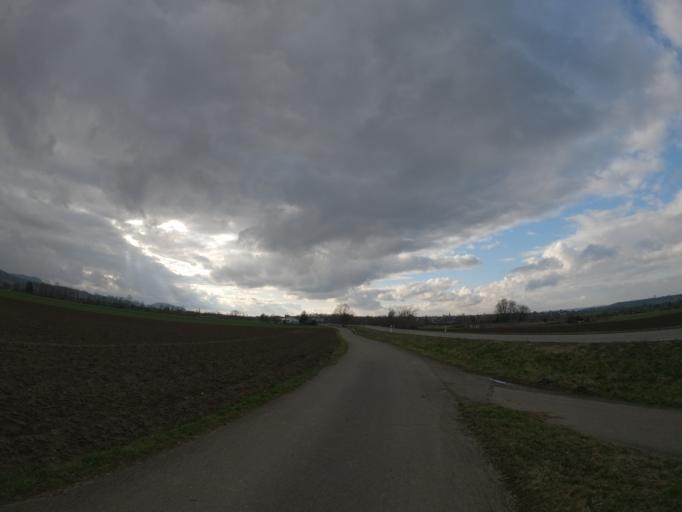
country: DE
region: Baden-Wuerttemberg
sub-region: Regierungsbezirk Stuttgart
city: Eschenbach
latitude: 48.6549
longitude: 9.6648
